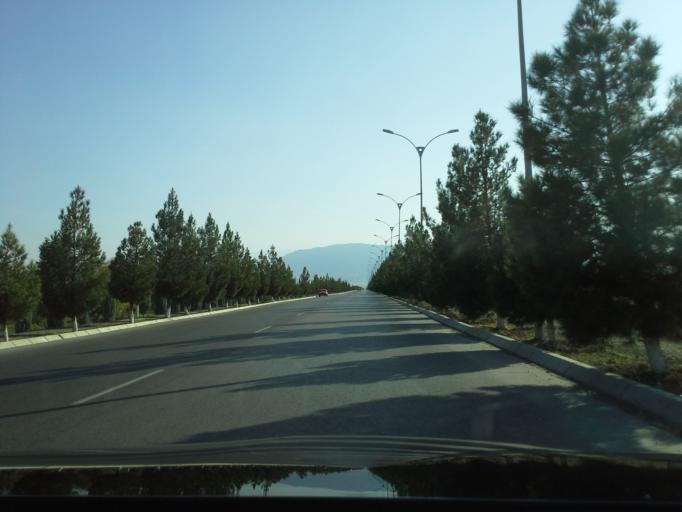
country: TM
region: Ahal
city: Abadan
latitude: 38.1603
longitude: 58.0940
